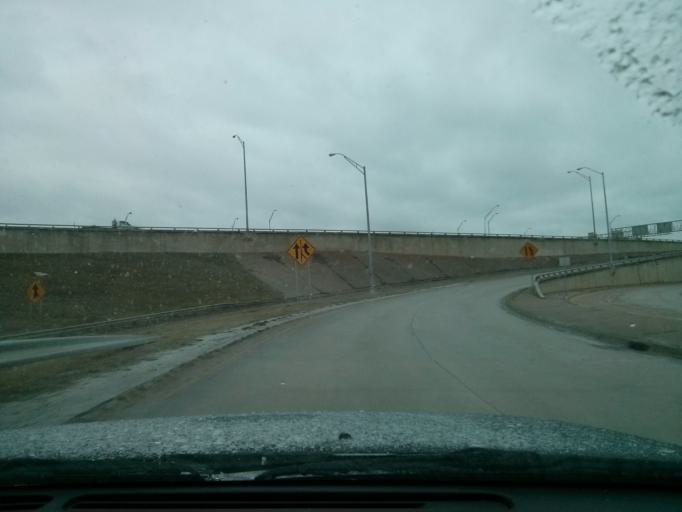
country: US
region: Oklahoma
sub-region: Tulsa County
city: Tulsa
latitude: 36.1580
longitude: -95.9793
